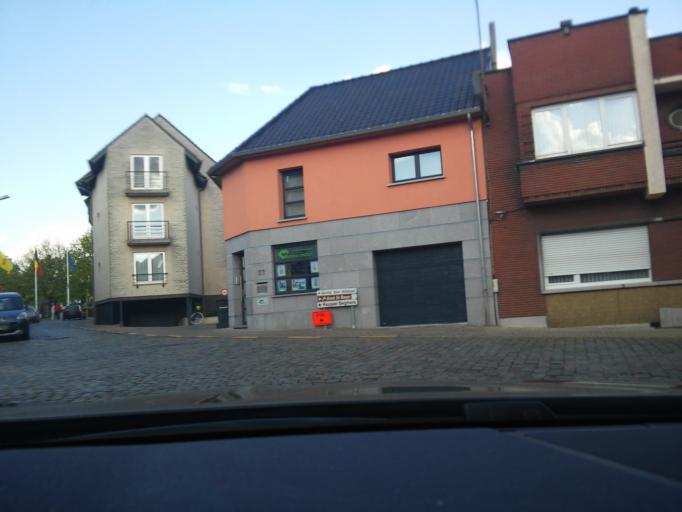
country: BE
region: Flanders
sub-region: Provincie Antwerpen
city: Boom
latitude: 51.0808
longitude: 4.3652
